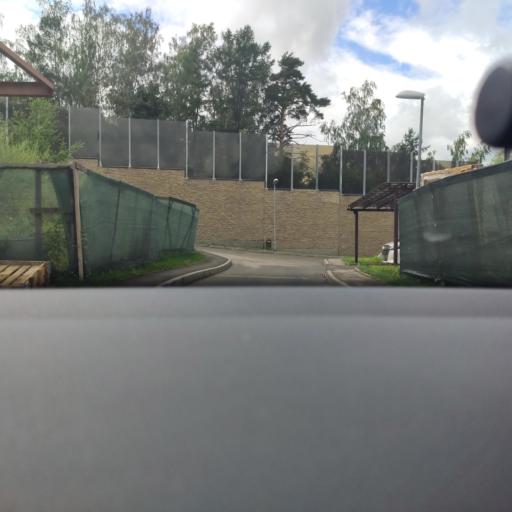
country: RU
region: Moscow
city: Rublevo
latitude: 55.8048
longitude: 37.3786
